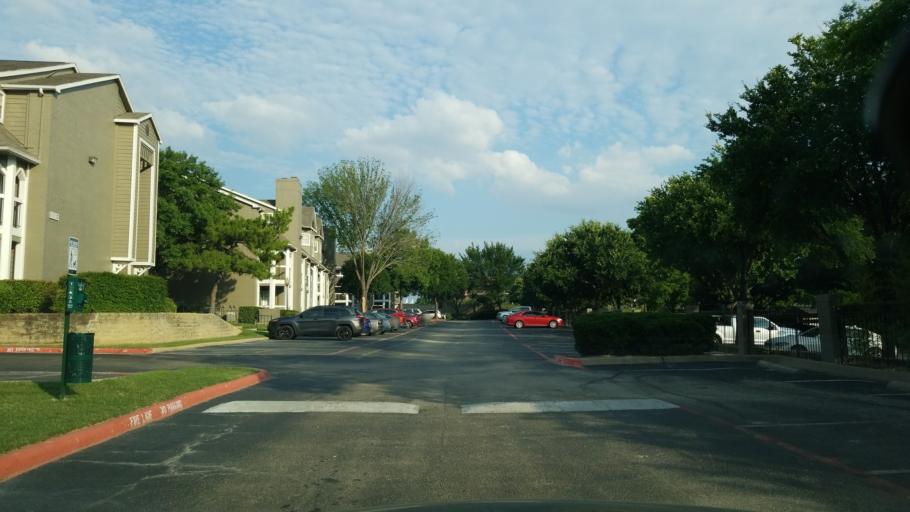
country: US
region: Texas
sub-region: Dallas County
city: Coppell
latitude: 32.9026
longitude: -96.9651
